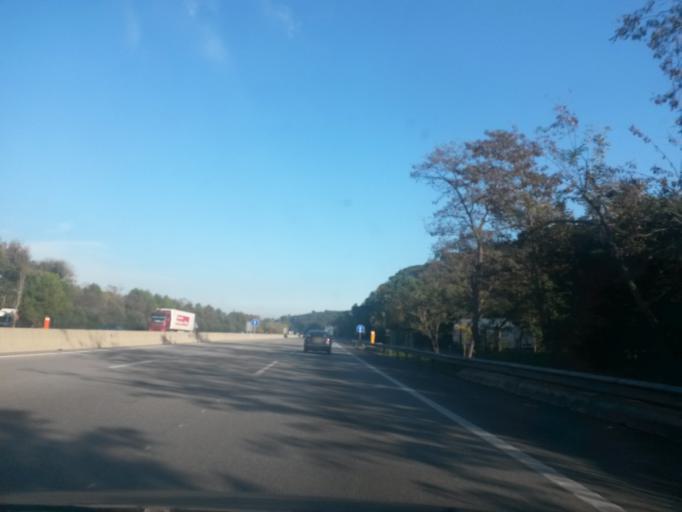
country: ES
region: Catalonia
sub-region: Provincia de Girona
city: Breda
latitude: 41.7257
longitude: 2.5918
